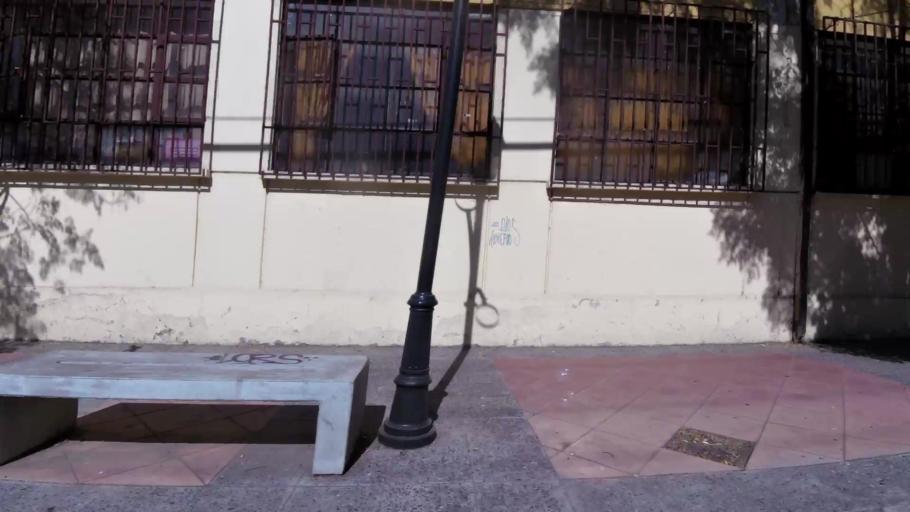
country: CL
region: Maule
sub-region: Provincia de Talca
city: Talca
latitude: -35.4298
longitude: -71.6656
